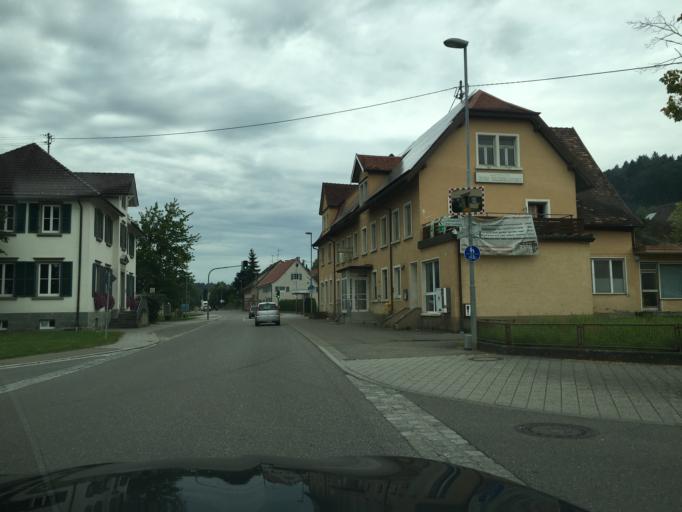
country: DE
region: Baden-Wuerttemberg
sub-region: Freiburg Region
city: Bodman-Ludwigshafen
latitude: 47.8563
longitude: 9.0593
